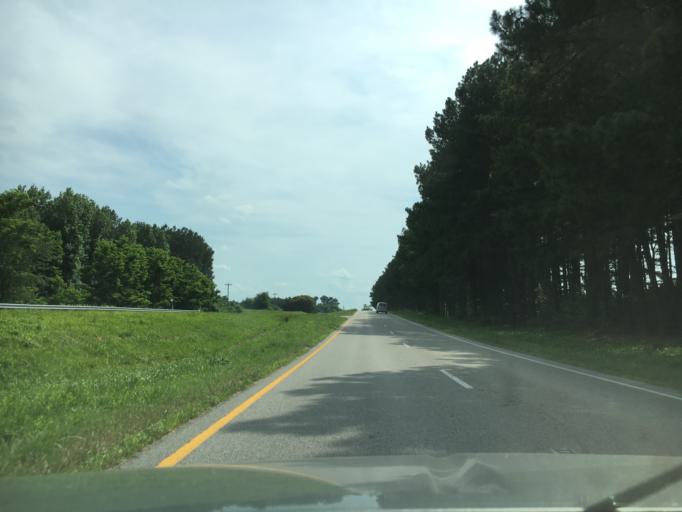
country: US
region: Virginia
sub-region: Nottoway County
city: Crewe
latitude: 37.2047
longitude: -78.1670
